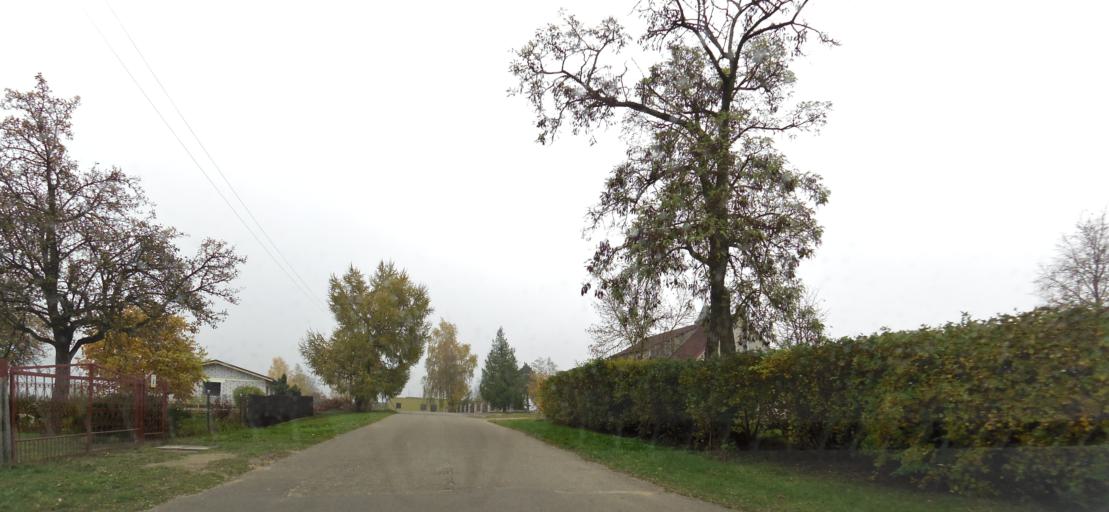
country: BY
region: Grodnenskaya
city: Astravyets
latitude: 54.6372
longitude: 25.6866
